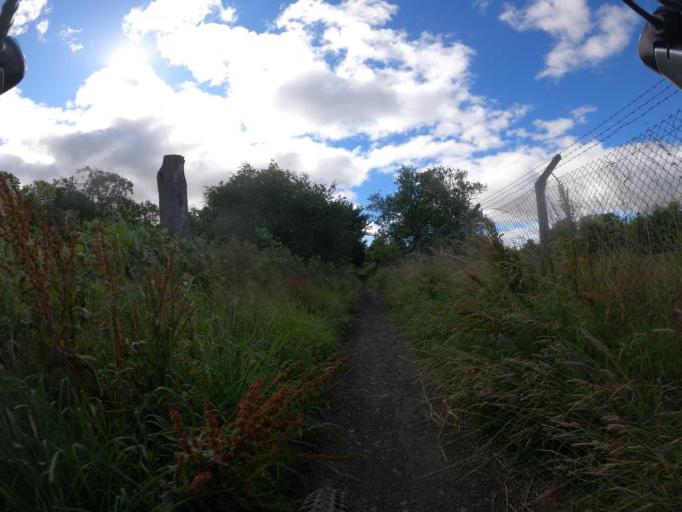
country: GB
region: Scotland
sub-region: Edinburgh
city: Edinburgh
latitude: 55.9758
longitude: -3.2603
